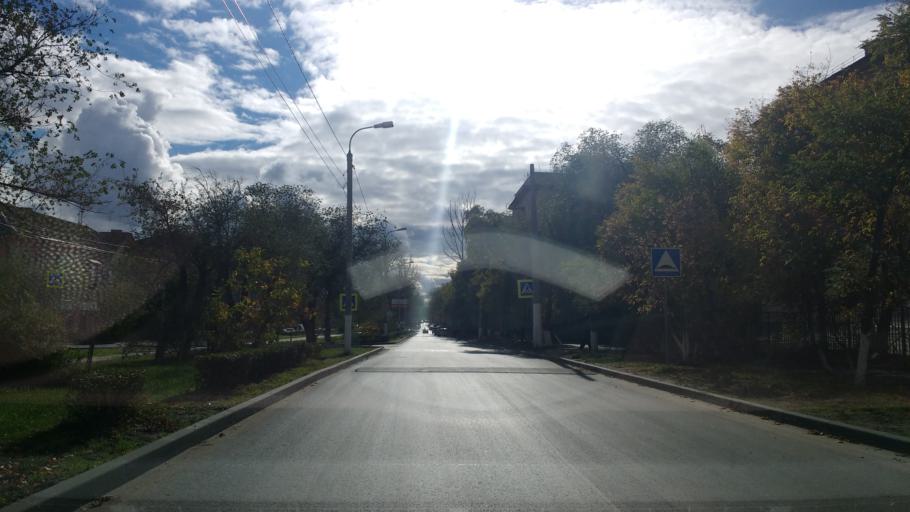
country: RU
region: Volgograd
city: Krasnoslobodsk
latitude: 48.7694
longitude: 44.5563
